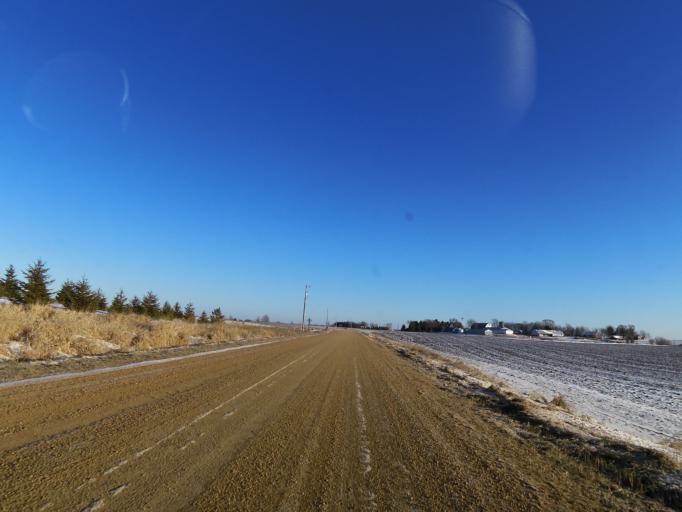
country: US
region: Minnesota
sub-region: Scott County
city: Jordan
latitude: 44.6759
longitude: -93.5371
